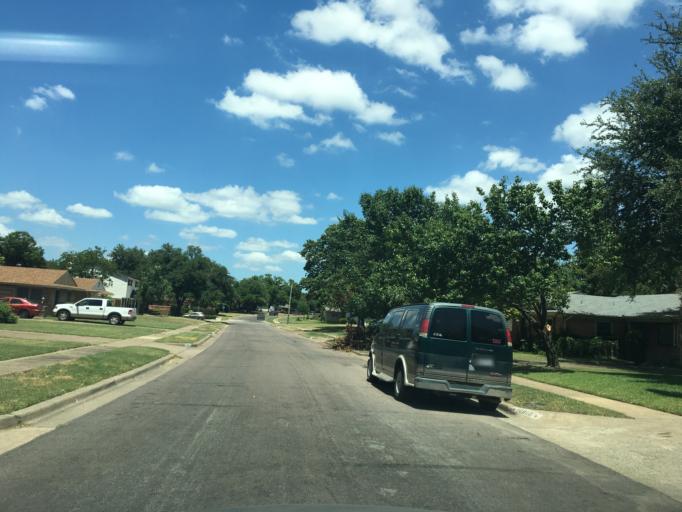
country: US
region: Texas
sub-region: Dallas County
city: Garland
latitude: 32.8497
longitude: -96.6908
